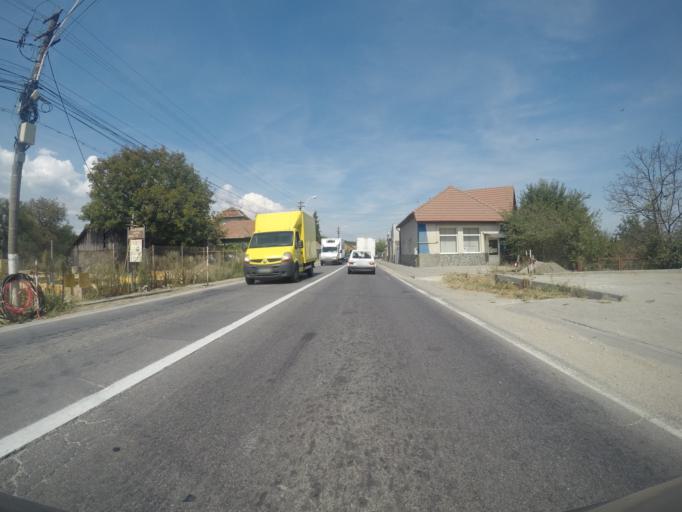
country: RO
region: Alba
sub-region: Oras Teius
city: Teius
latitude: 46.2033
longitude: 23.6717
